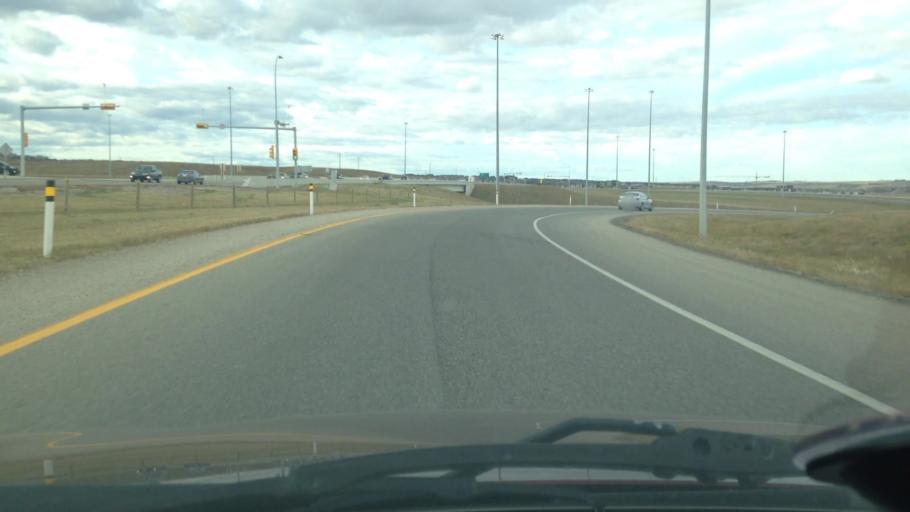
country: CA
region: Alberta
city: Calgary
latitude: 51.1502
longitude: -114.1387
